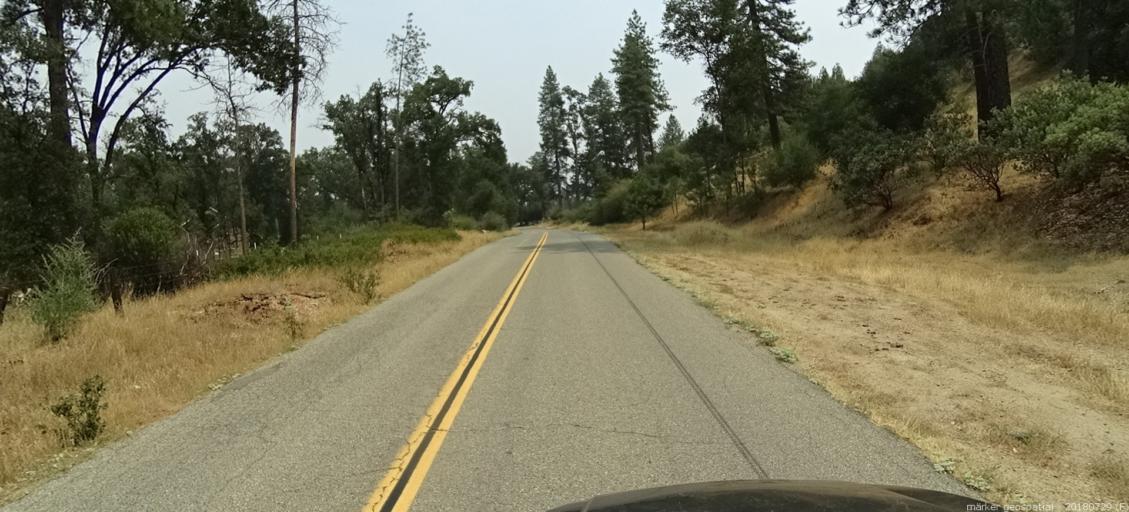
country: US
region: California
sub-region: Madera County
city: Ahwahnee
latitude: 37.3503
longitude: -119.7385
